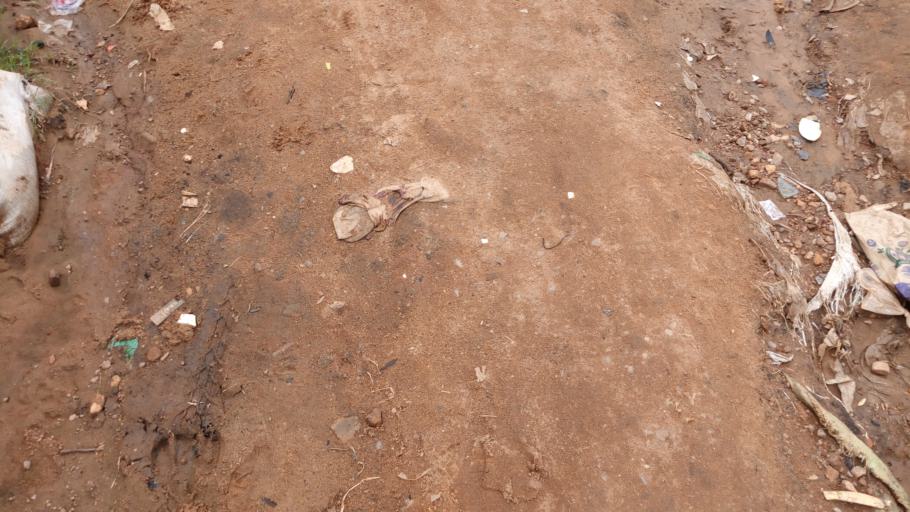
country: UG
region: Central Region
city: Kampala Central Division
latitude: 0.3580
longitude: 32.5611
